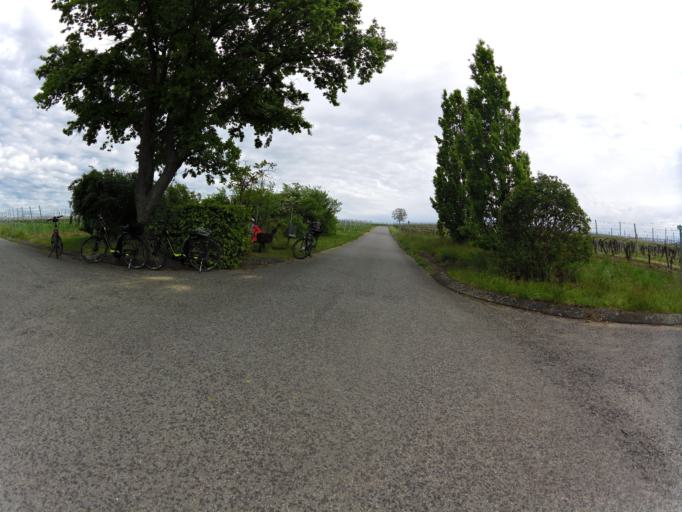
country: DE
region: Bavaria
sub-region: Regierungsbezirk Unterfranken
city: Nordheim
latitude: 49.8534
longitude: 10.1851
